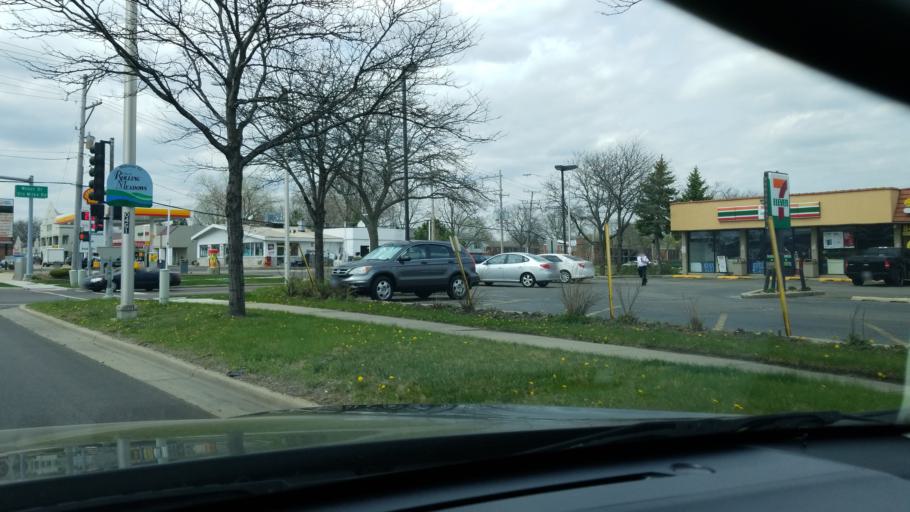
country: US
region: Illinois
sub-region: Cook County
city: Rolling Meadows
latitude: 42.0579
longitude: -88.0066
